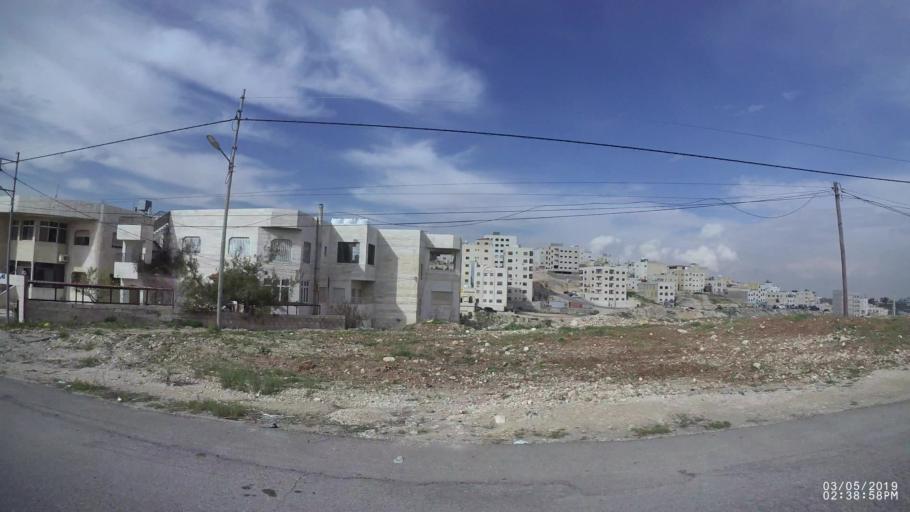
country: JO
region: Amman
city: Amman
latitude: 32.0102
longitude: 35.9414
